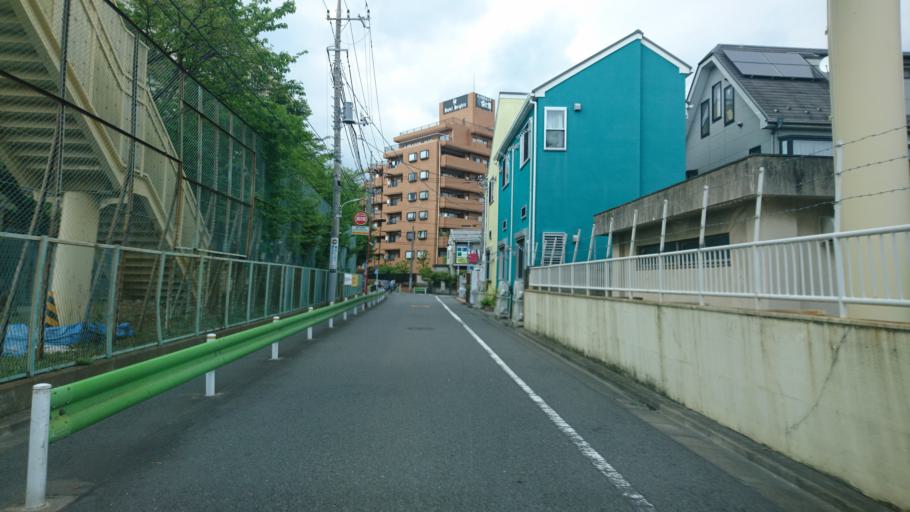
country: JP
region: Kanagawa
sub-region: Kawasaki-shi
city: Kawasaki
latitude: 35.5457
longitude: 139.7174
